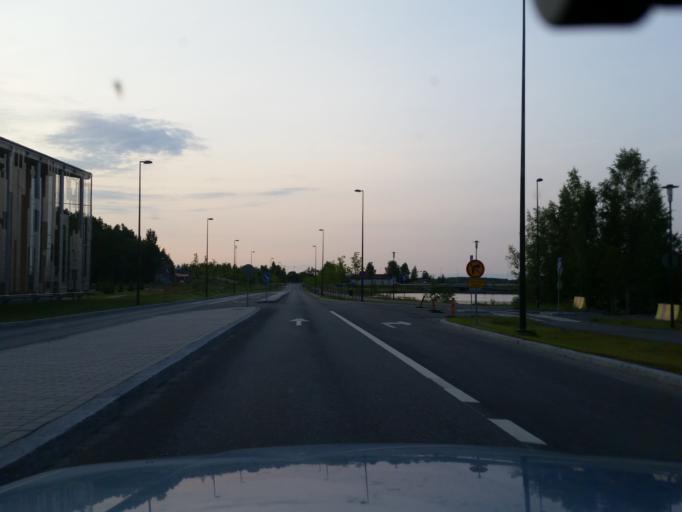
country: FI
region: Southern Savonia
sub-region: Savonlinna
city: Savonlinna
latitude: 61.8722
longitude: 28.8753
